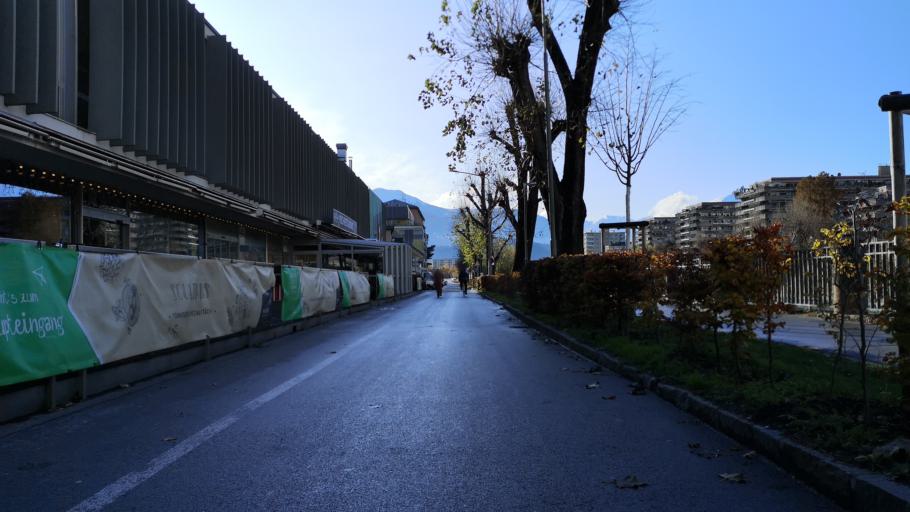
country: AT
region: Tyrol
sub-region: Innsbruck Stadt
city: Innsbruck
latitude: 47.2675
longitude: 11.3898
